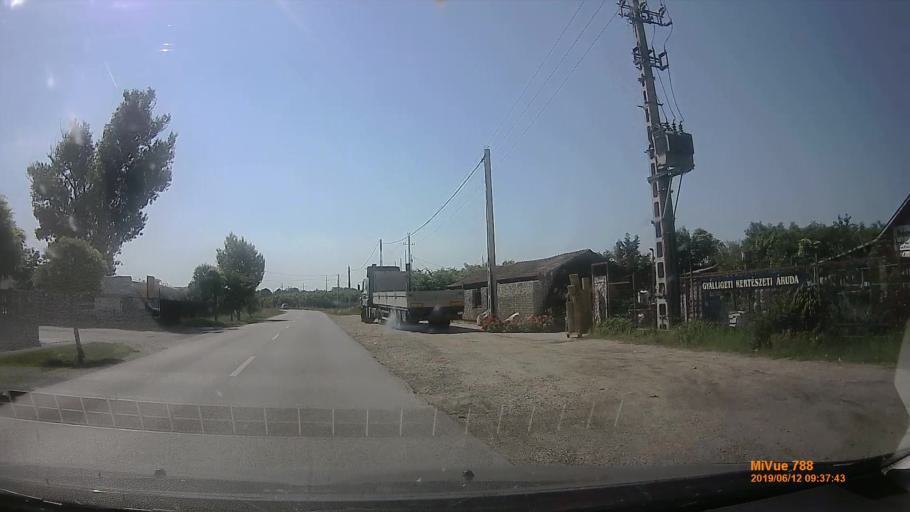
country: HU
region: Pest
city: Gyal
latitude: 47.3737
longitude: 19.2256
